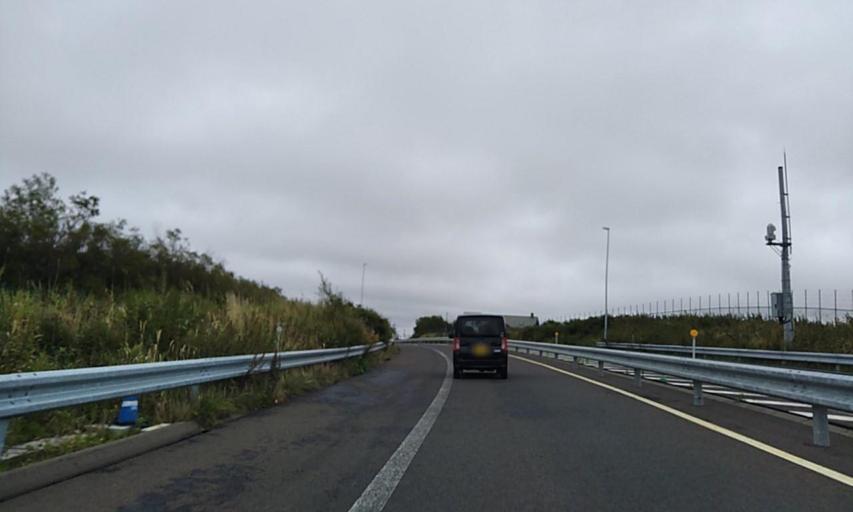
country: JP
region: Hokkaido
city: Nemuro
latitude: 43.3141
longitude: 145.5495
